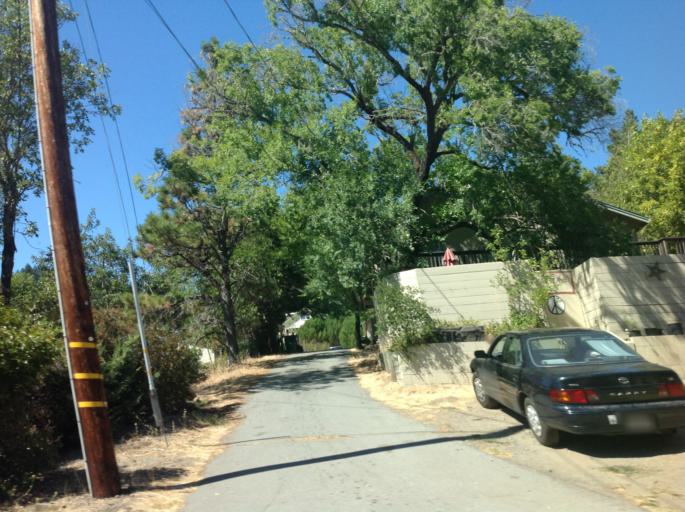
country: US
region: California
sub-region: Marin County
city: Lagunitas-Forest Knolls
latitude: 38.0153
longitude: -122.6913
